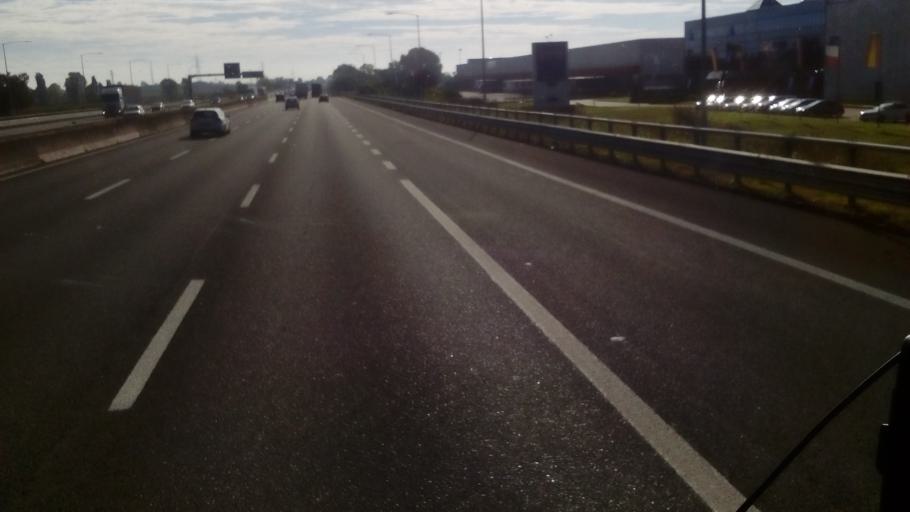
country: IT
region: Lombardy
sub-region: Citta metropolitana di Milano
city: Cerro al Lambro
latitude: 45.3377
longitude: 9.3328
